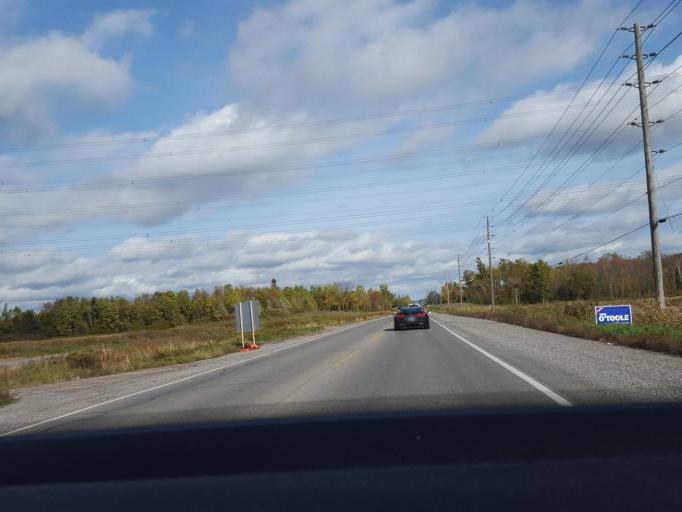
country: CA
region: Ontario
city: Oshawa
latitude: 43.9596
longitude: -78.7629
